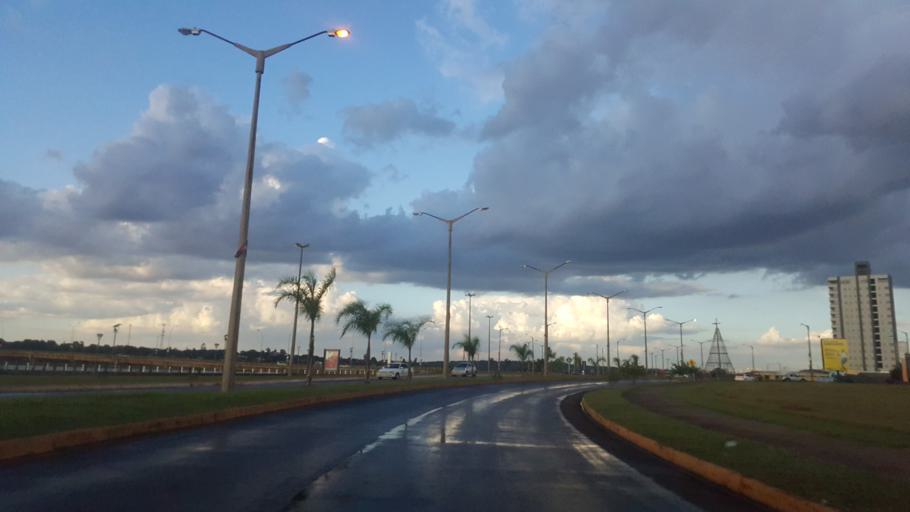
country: PY
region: Itapua
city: Encarnacion
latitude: -27.3224
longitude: -55.8758
